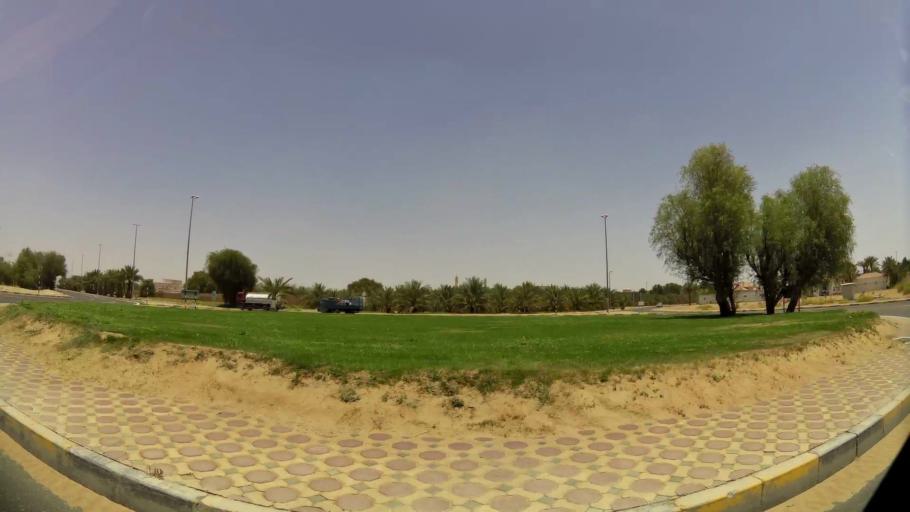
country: OM
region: Al Buraimi
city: Al Buraymi
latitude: 24.2702
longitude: 55.7054
